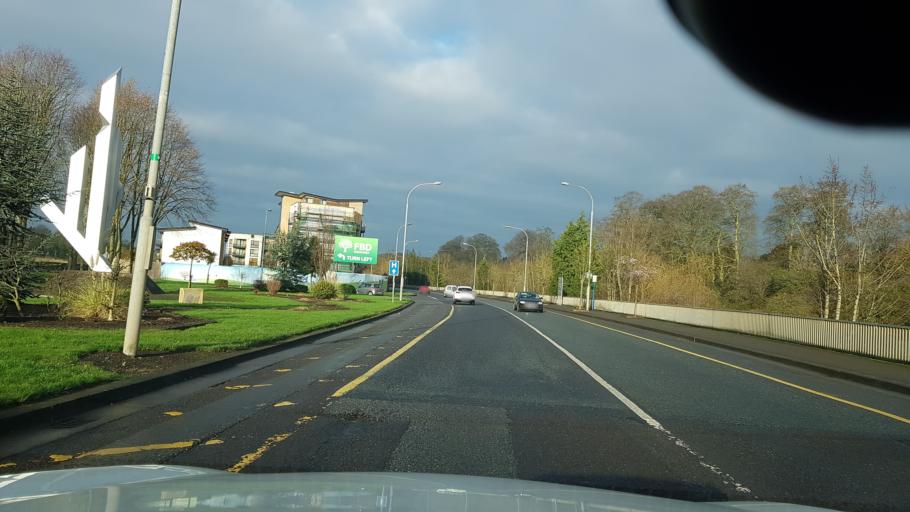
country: IE
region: Leinster
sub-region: An Mhi
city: Navan
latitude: 53.6452
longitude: -6.6735
